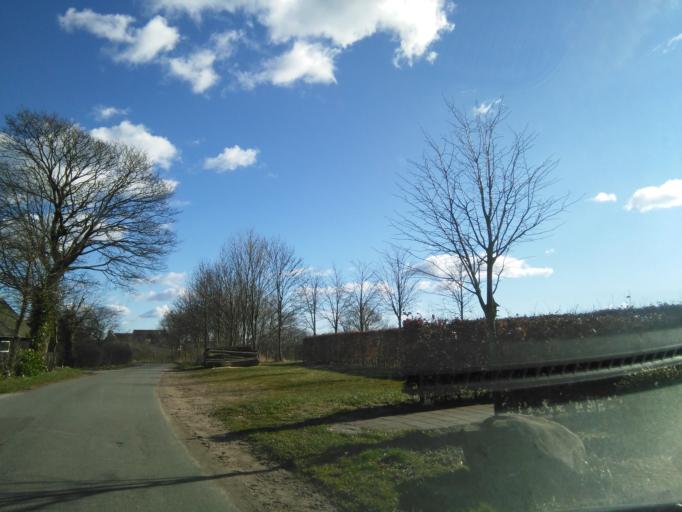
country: DK
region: Central Jutland
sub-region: Arhus Kommune
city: Beder
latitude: 56.0658
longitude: 10.2328
